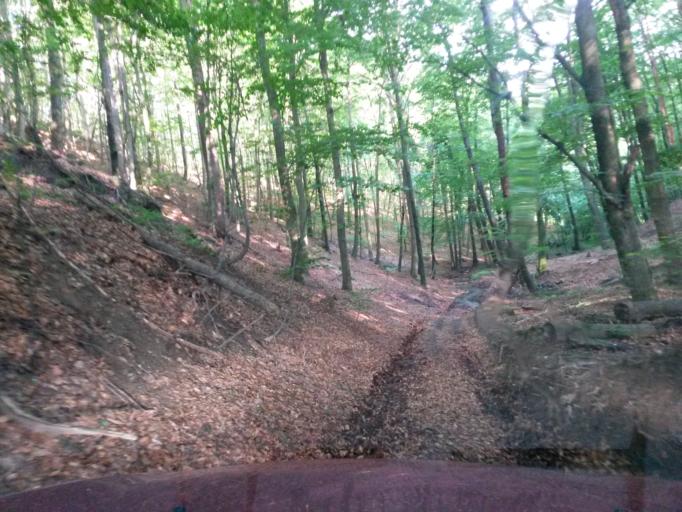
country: SK
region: Kosicky
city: Moldava nad Bodvou
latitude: 48.7282
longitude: 21.0752
